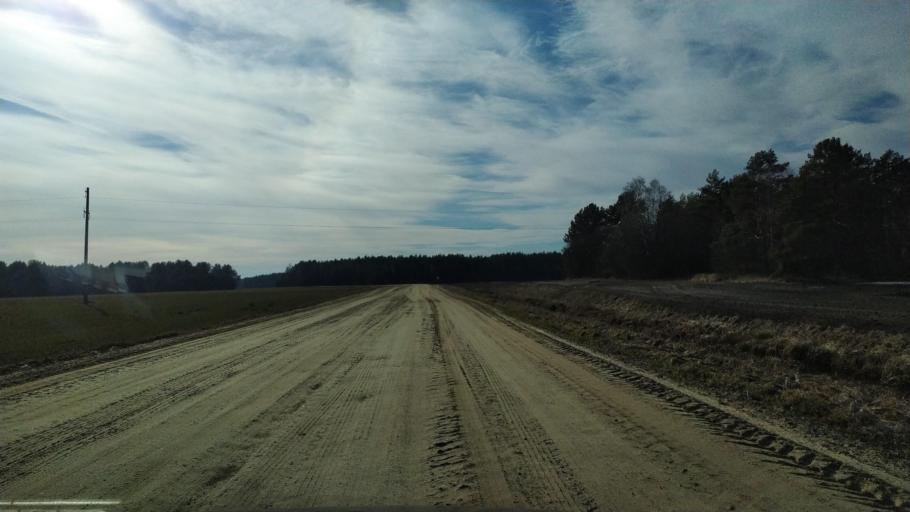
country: BY
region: Brest
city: Pruzhany
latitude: 52.5729
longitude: 24.3000
